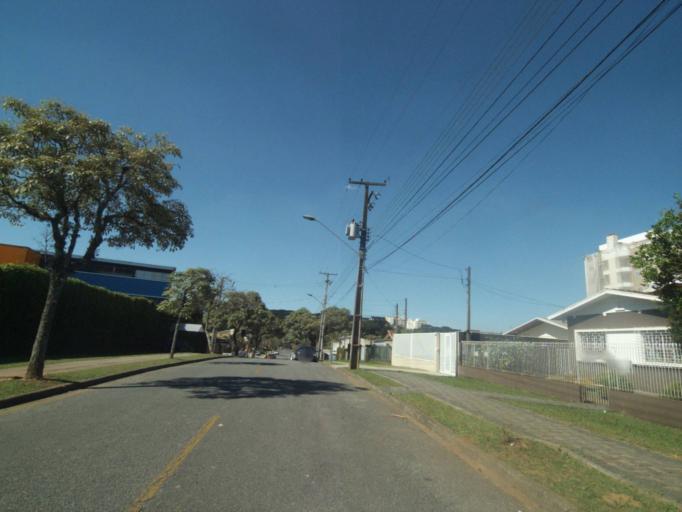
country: BR
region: Parana
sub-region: Curitiba
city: Curitiba
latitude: -25.3915
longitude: -49.2345
